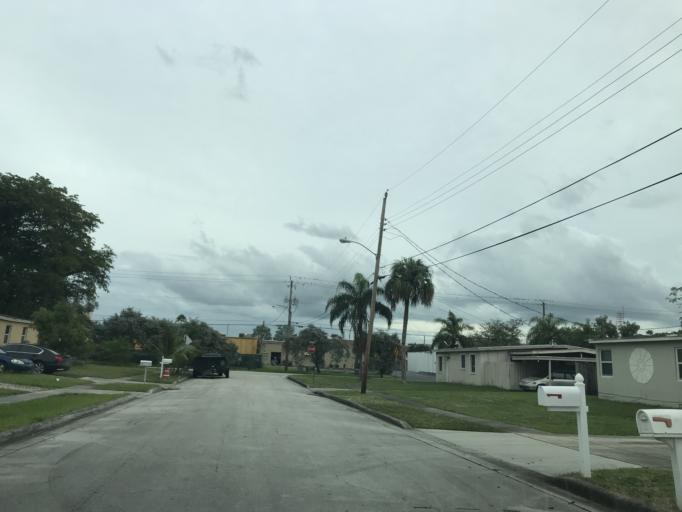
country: US
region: Florida
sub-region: Broward County
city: Margate
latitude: 26.2524
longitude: -80.2032
